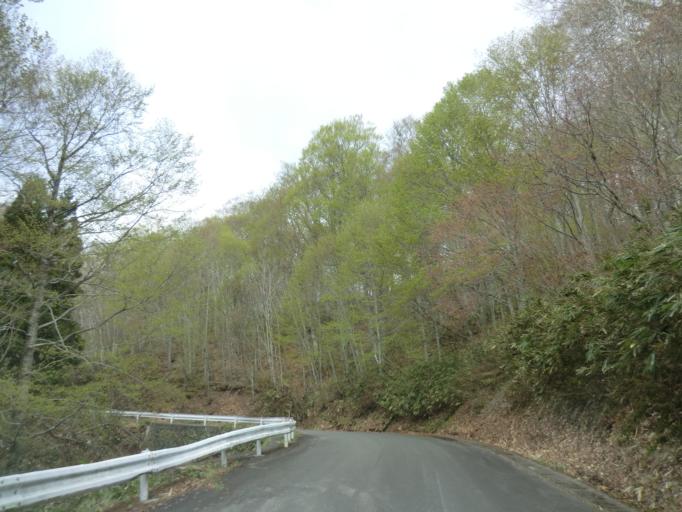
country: JP
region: Aomori
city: Mutsu
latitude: 41.3372
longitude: 141.0724
